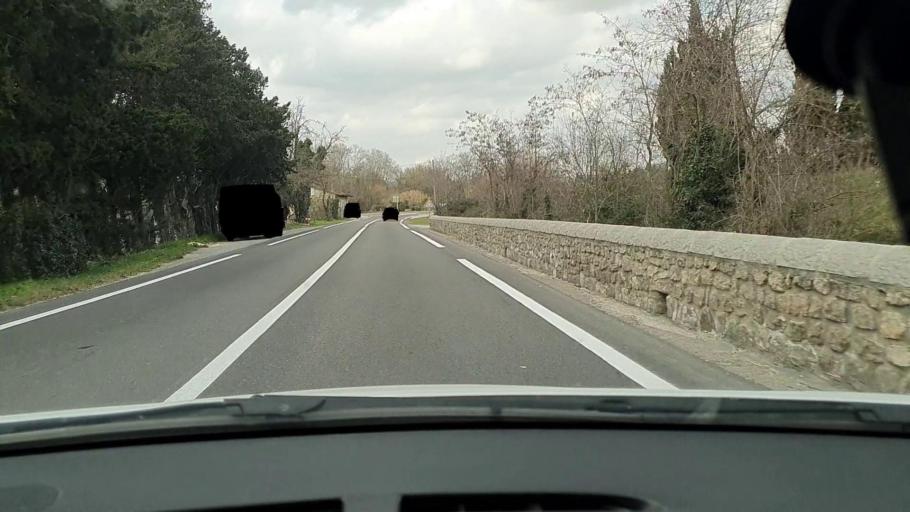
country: FR
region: Languedoc-Roussillon
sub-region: Departement du Gard
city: Meynes
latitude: 43.8789
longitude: 4.5769
